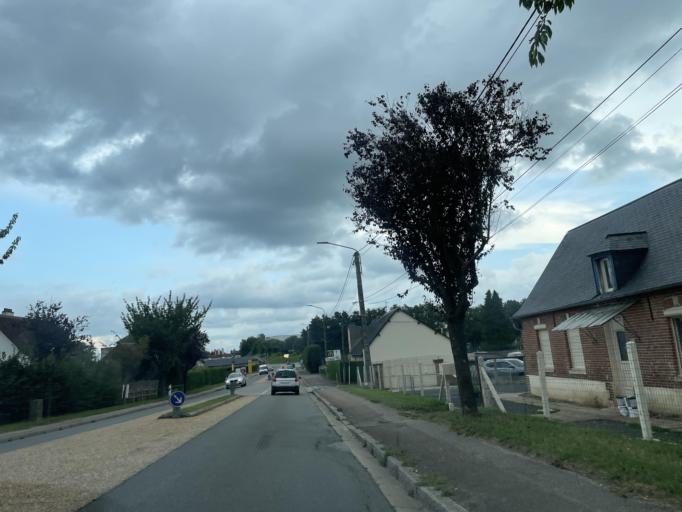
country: FR
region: Haute-Normandie
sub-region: Departement de la Seine-Maritime
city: Gournay-en-Bray
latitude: 49.4841
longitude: 1.7095
